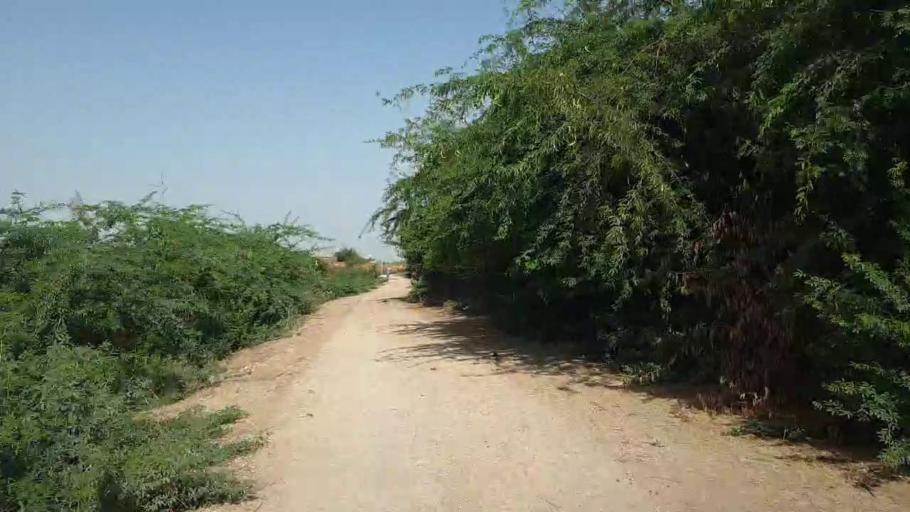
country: PK
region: Sindh
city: Tando Bago
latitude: 24.7534
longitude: 69.0280
